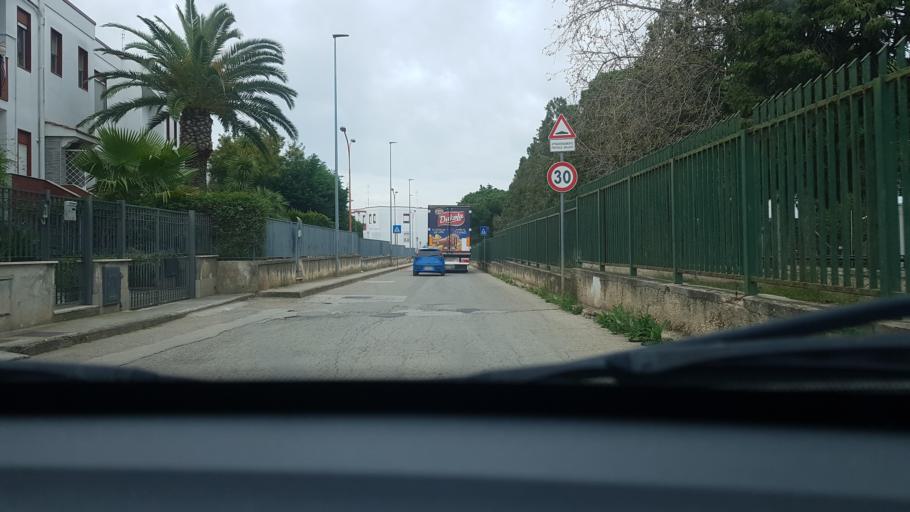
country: IT
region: Apulia
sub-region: Provincia di Bari
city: Noicattaro
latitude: 41.0355
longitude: 16.9832
